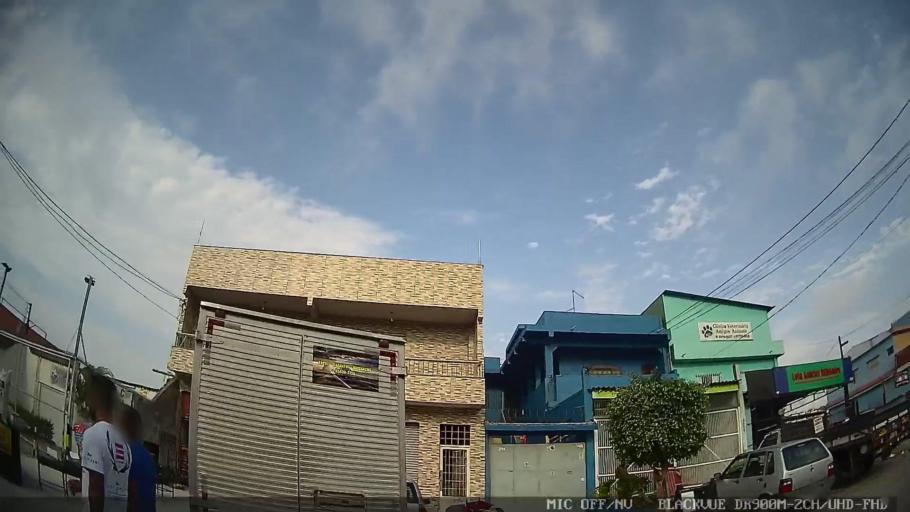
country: BR
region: Sao Paulo
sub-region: Ferraz De Vasconcelos
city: Ferraz de Vasconcelos
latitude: -23.5200
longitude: -46.3996
